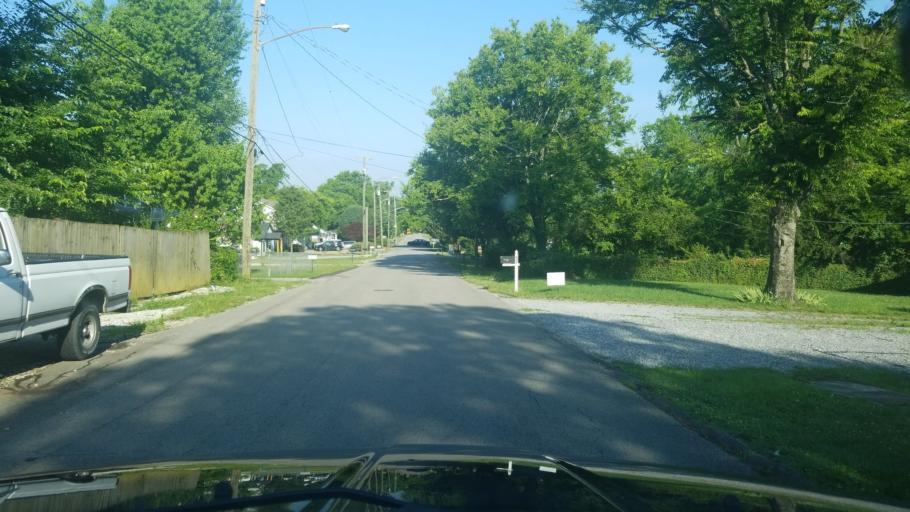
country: US
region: Tennessee
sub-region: Davidson County
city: Oak Hill
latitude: 36.1019
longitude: -86.7458
